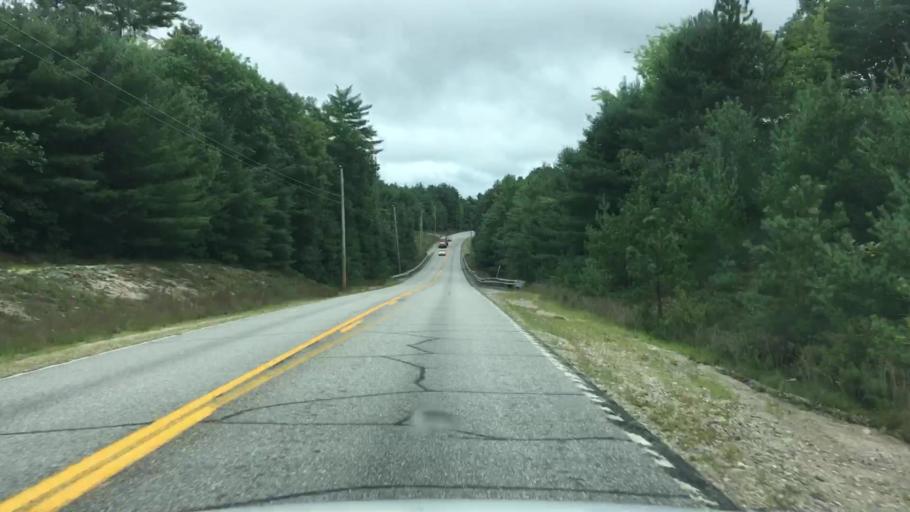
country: US
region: Maine
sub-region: Oxford County
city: Hiram
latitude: 43.8984
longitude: -70.8326
